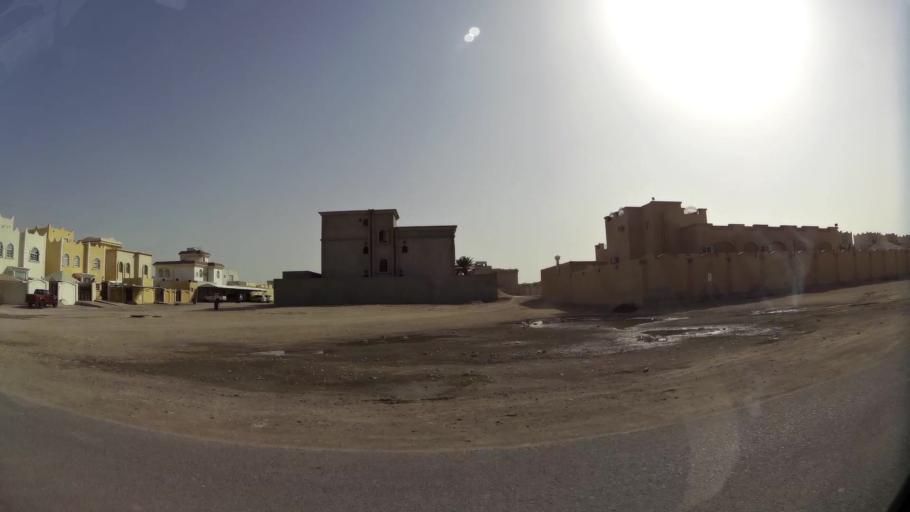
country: QA
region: Baladiyat ar Rayyan
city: Ar Rayyan
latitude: 25.3346
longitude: 51.4243
